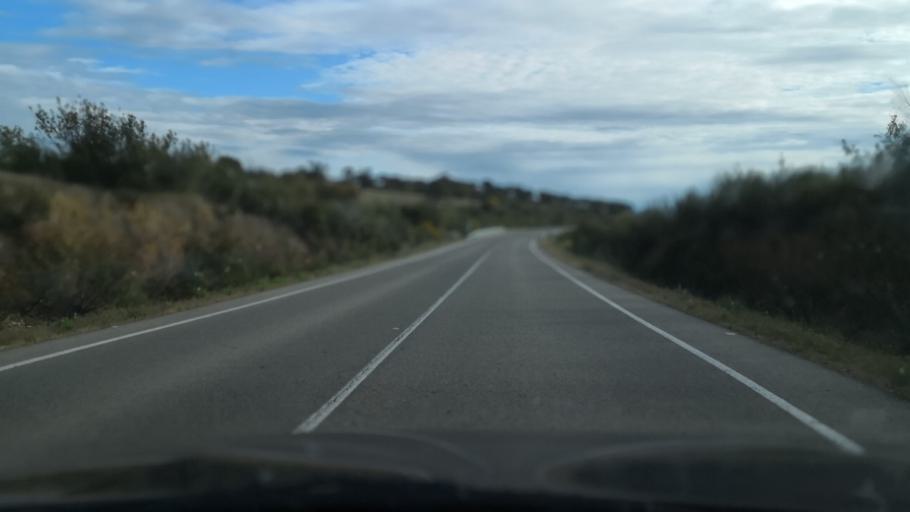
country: ES
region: Extremadura
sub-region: Provincia de Caceres
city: Moraleja
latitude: 40.1075
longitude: -6.6741
